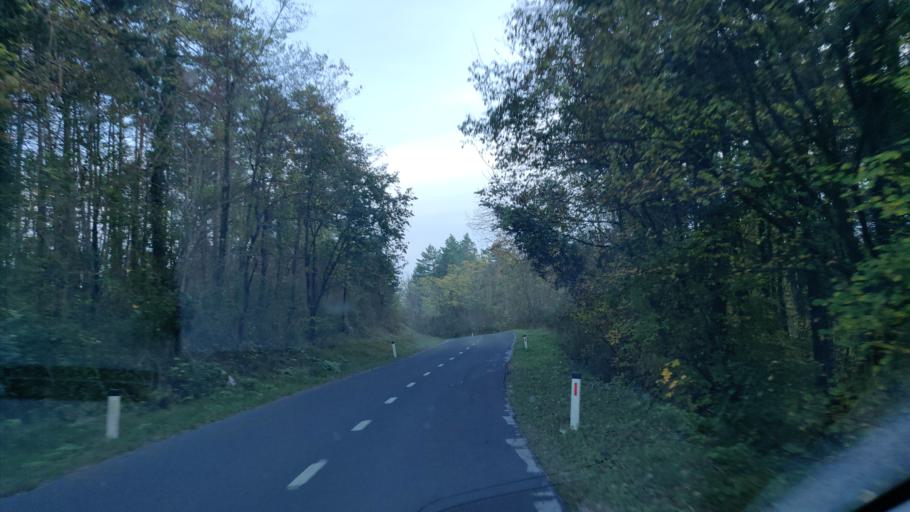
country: SI
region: Sezana
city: Sezana
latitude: 45.7692
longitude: 13.8796
